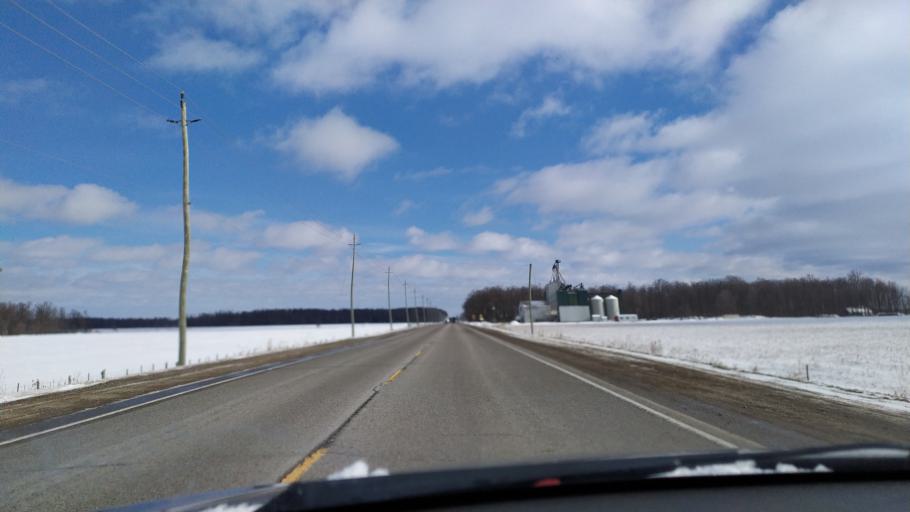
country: CA
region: Ontario
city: Waterloo
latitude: 43.5797
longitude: -80.6038
